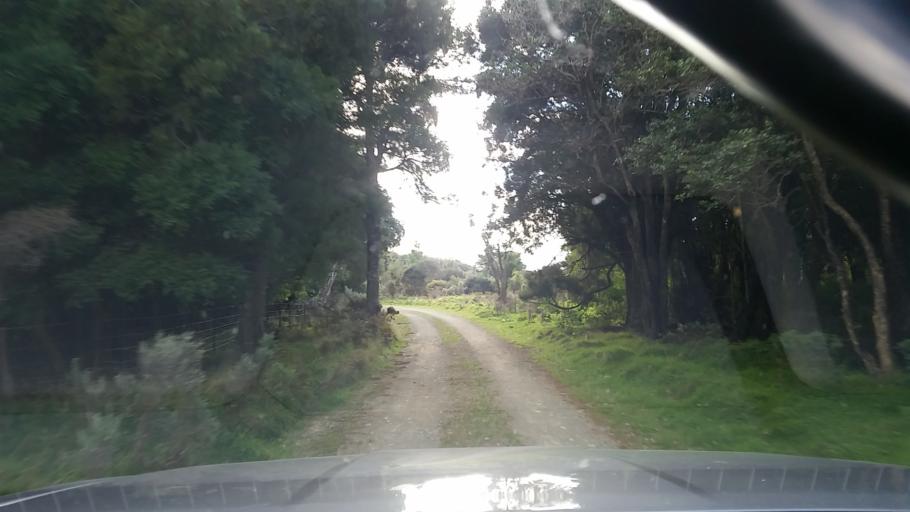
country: NZ
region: Marlborough
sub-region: Marlborough District
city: Picton
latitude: -41.0562
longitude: 174.1104
